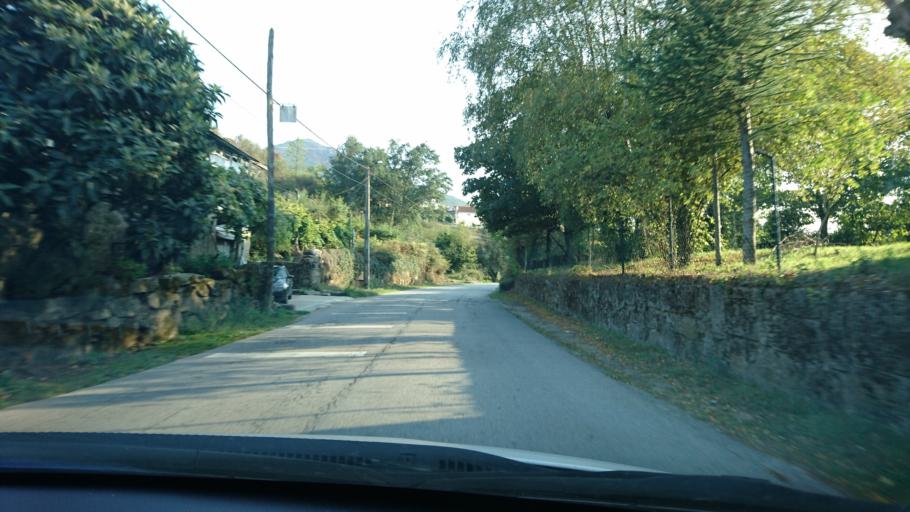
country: PT
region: Vila Real
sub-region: Mondim de Basto
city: Mondim de Basto
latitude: 41.4434
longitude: -7.9261
